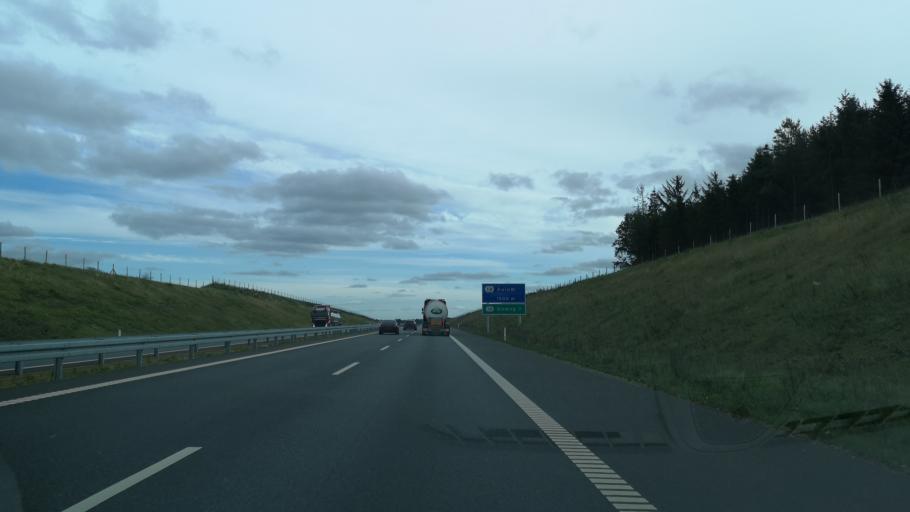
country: DK
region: Central Jutland
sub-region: Herning Kommune
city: Avlum
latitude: 56.2680
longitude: 8.7568
